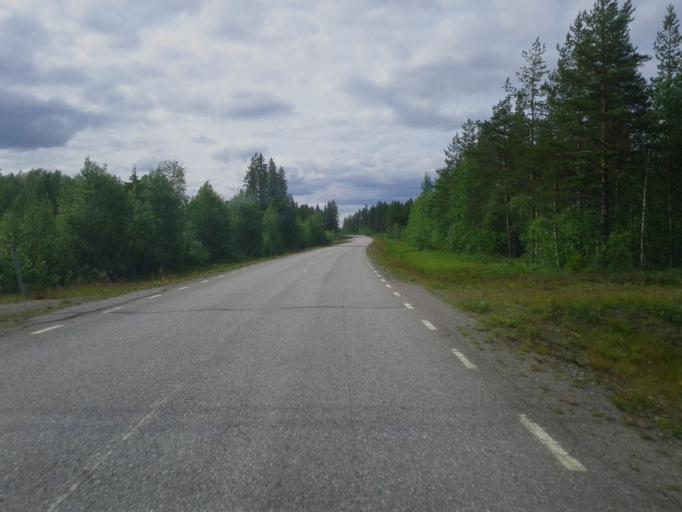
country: SE
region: Vaesterbotten
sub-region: Sorsele Kommun
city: Sorsele
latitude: 65.2816
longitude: 17.8861
